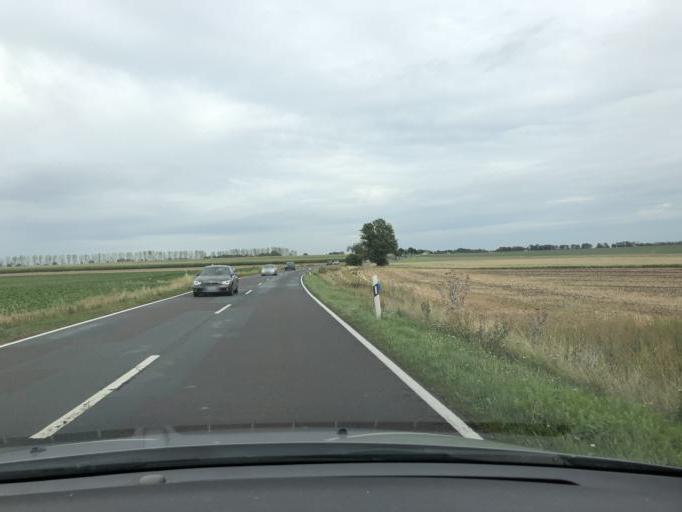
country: DE
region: Saxony-Anhalt
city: Wanzleben
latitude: 52.0676
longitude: 11.4557
